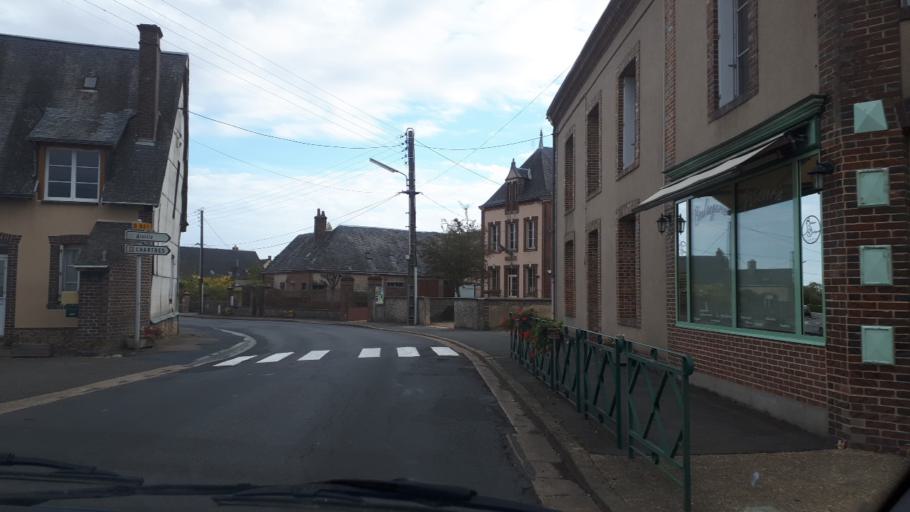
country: FR
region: Centre
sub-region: Departement du Loir-et-Cher
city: Mondoubleau
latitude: 48.0357
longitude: 0.9270
